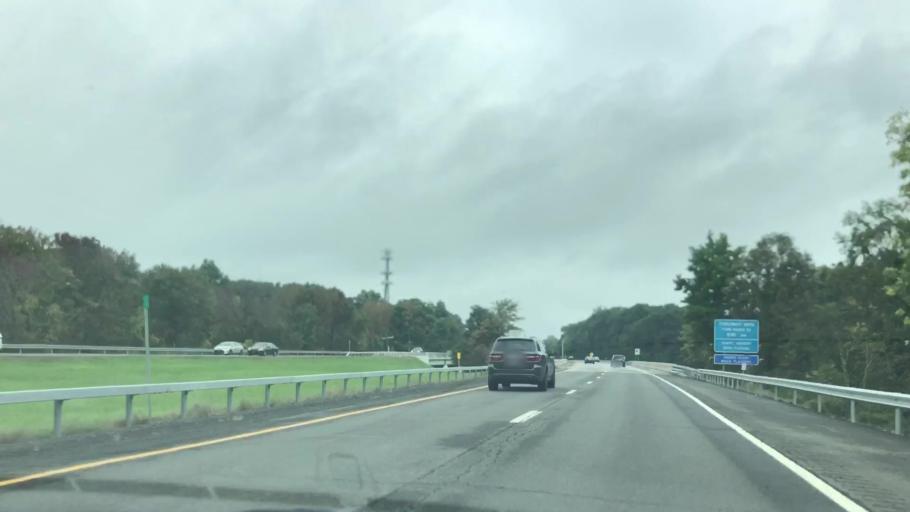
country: US
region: New York
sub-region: Rockland County
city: Chestnut Ridge
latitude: 41.0688
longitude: -74.0544
